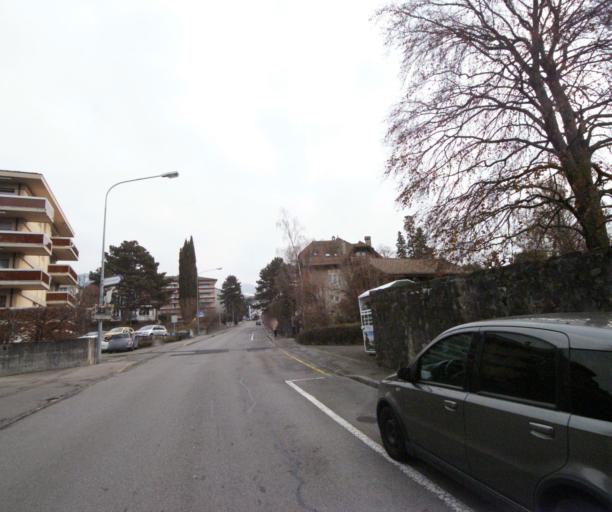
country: CH
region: Vaud
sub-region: Riviera-Pays-d'Enhaut District
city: La Tour-de-Peilz
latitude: 46.4586
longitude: 6.8593
